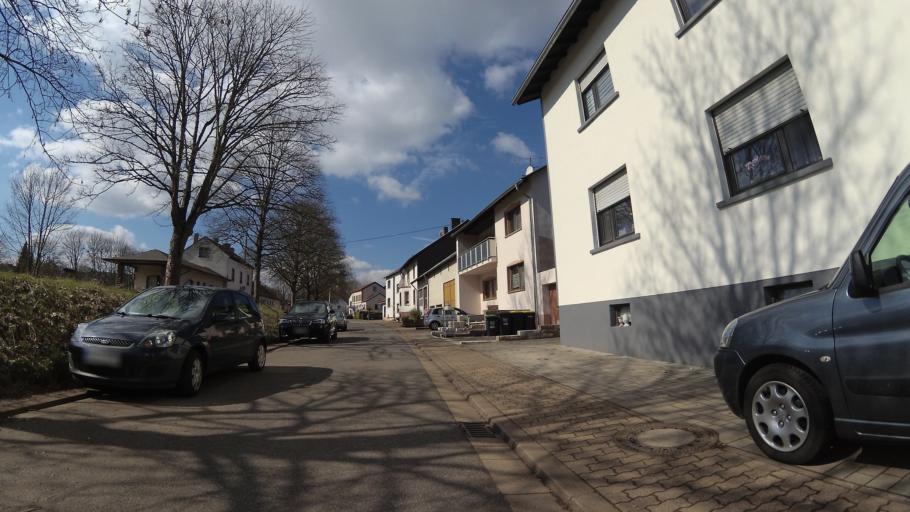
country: DE
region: Saarland
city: Rehlingen-Siersburg
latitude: 49.3545
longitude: 6.6165
